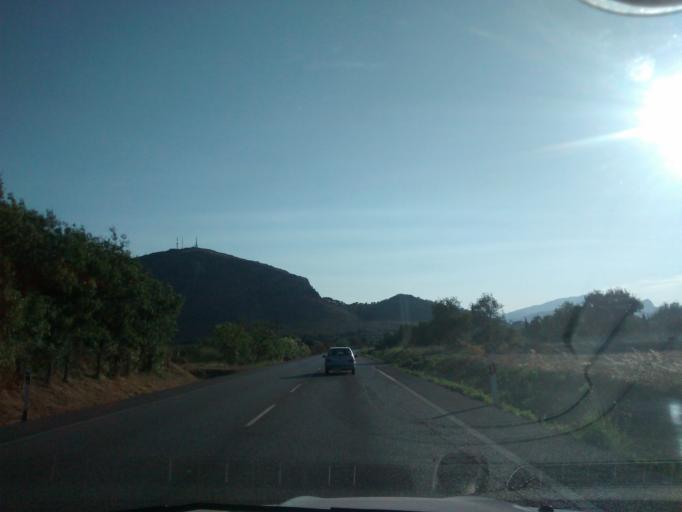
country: ES
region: Balearic Islands
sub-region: Illes Balears
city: Alcudia
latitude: 39.8432
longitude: 3.1111
